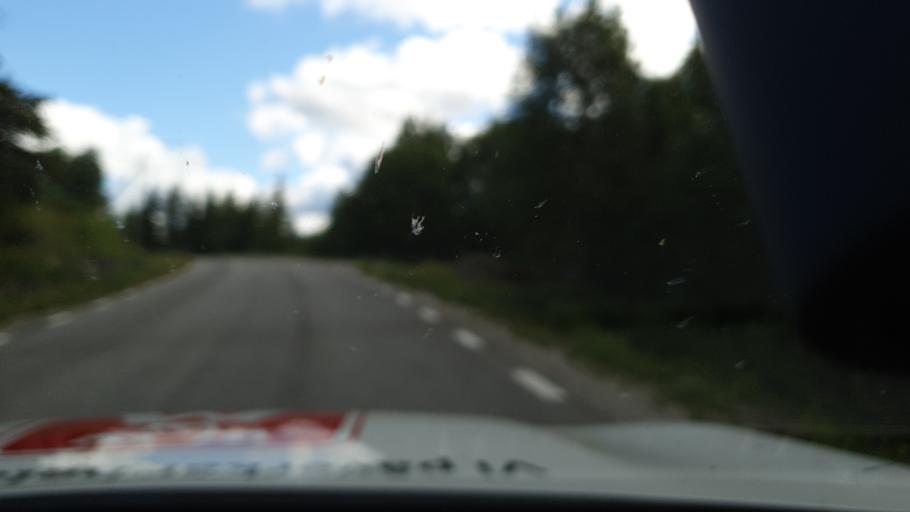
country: SE
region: Vaesterbotten
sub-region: Mala Kommun
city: Mala
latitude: 65.0248
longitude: 18.5297
